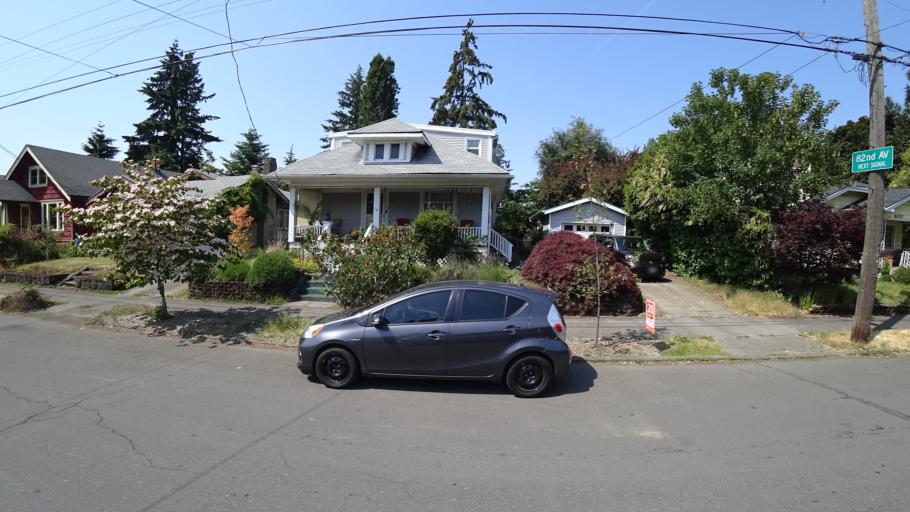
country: US
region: Oregon
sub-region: Multnomah County
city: Lents
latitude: 45.5162
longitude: -122.5805
